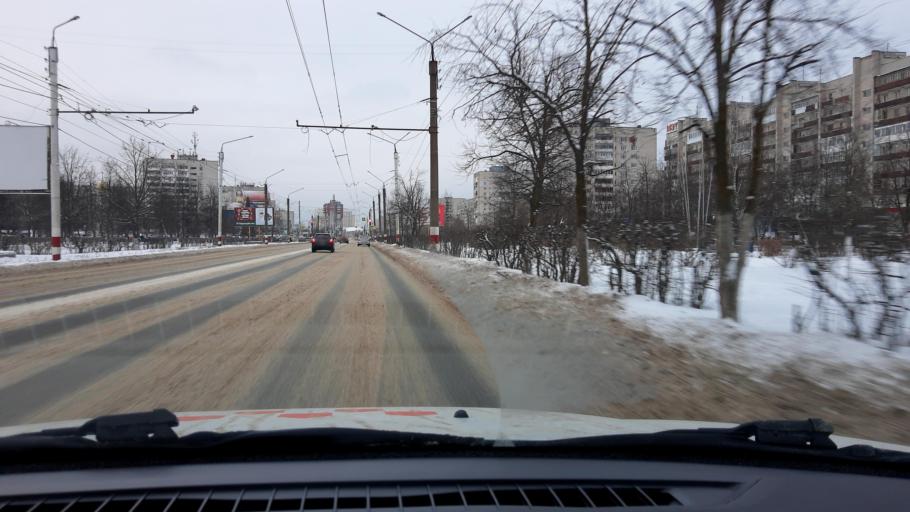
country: RU
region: Nizjnij Novgorod
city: Dzerzhinsk
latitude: 56.2268
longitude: 43.3948
